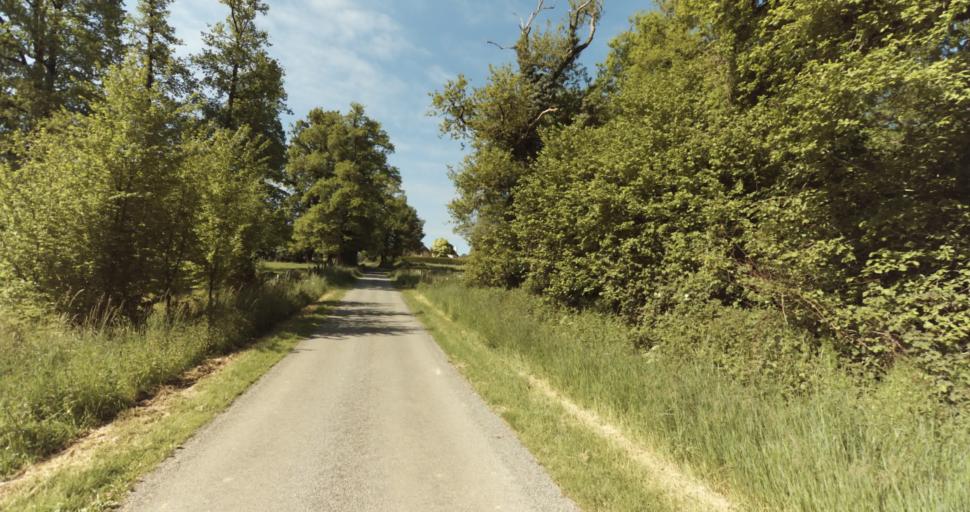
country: FR
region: Limousin
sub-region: Departement de la Haute-Vienne
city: Solignac
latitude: 45.6994
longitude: 1.2551
